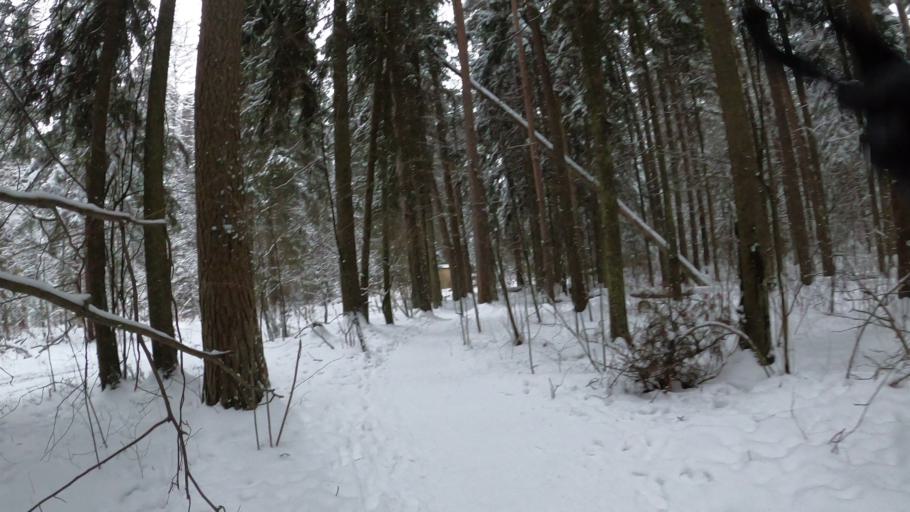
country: RU
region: Moskovskaya
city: Firsanovka
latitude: 55.9271
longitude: 37.2183
